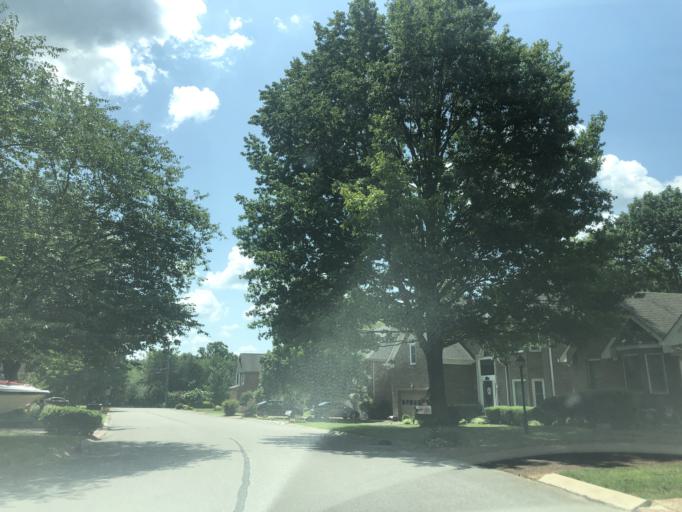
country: US
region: Tennessee
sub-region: Wilson County
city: Green Hill
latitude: 36.1556
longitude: -86.5881
